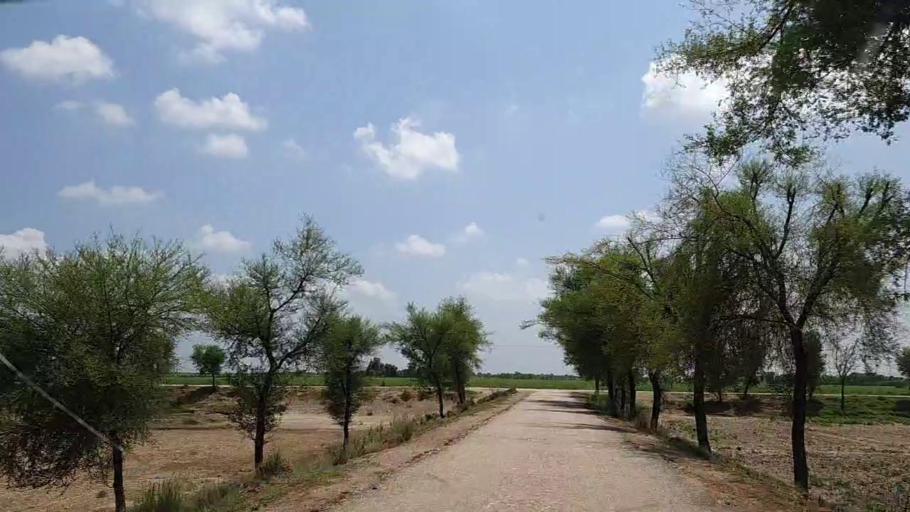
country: PK
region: Sindh
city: Tharu Shah
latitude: 27.0032
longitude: 68.0598
